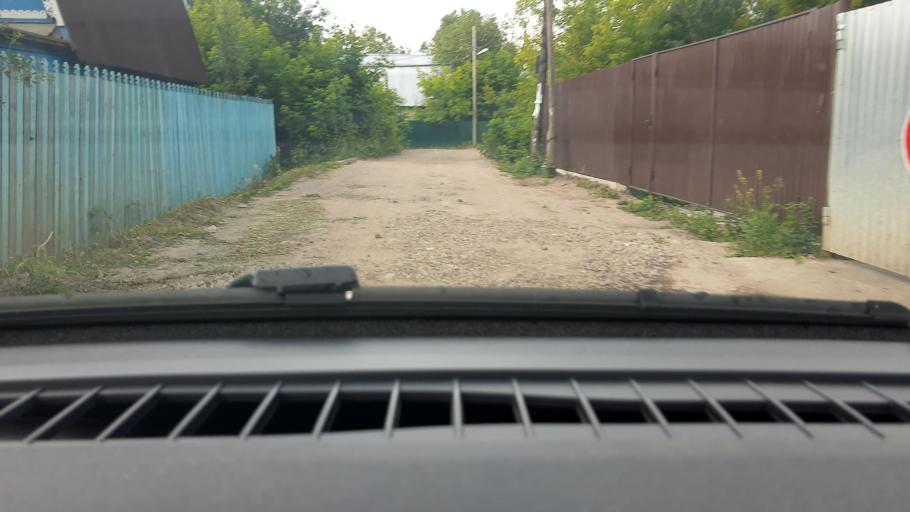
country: RU
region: Nizjnij Novgorod
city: Gorbatovka
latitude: 56.3135
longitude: 43.8307
